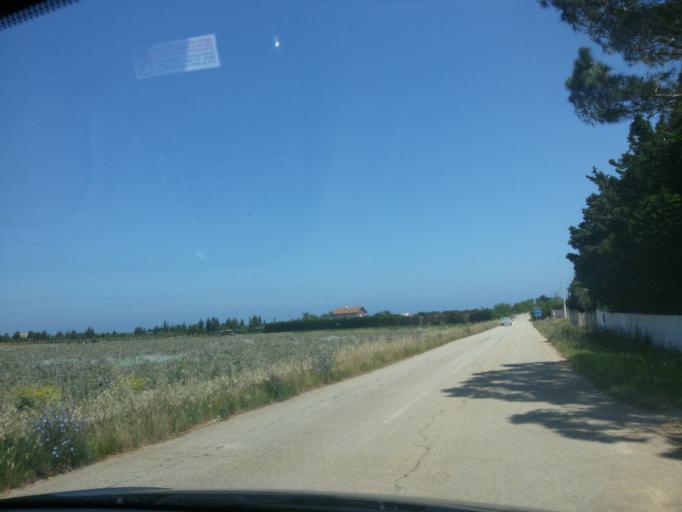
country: IT
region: Apulia
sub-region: Provincia di Brindisi
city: Brindisi
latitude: 40.6727
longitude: 17.8427
